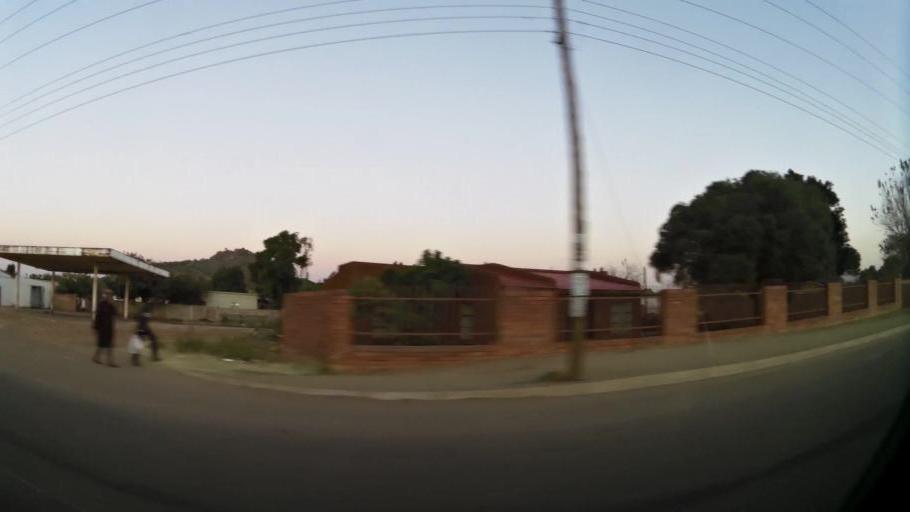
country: ZA
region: North-West
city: Ga-Rankuwa
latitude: -25.6049
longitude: 27.9705
